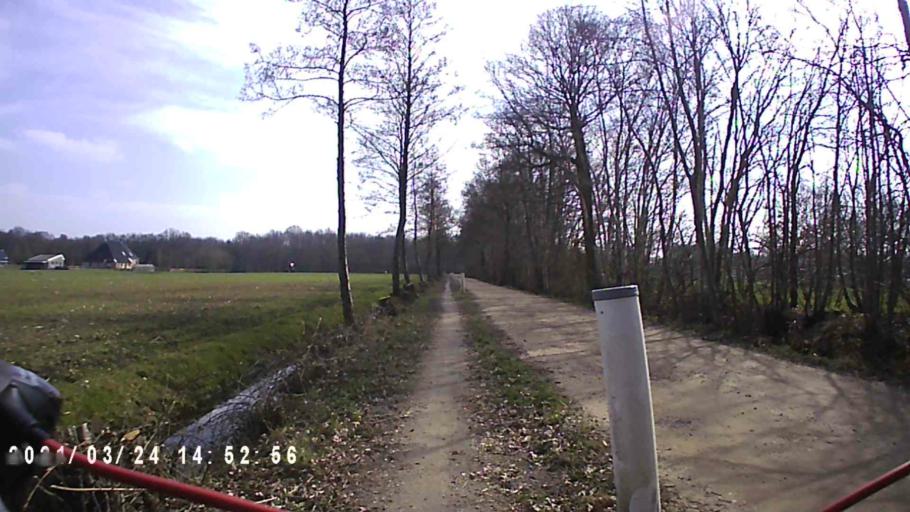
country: NL
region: Friesland
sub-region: Gemeente Heerenveen
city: Jubbega
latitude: 53.0271
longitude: 6.1037
